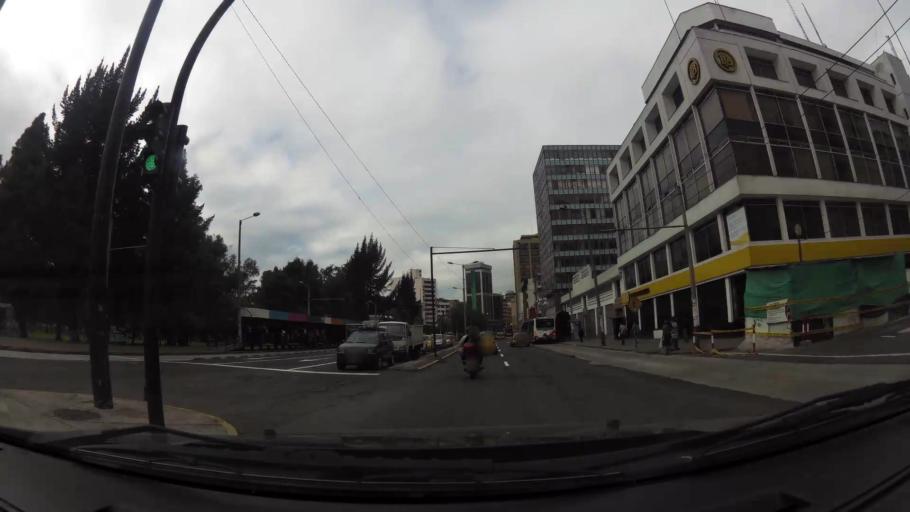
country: EC
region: Pichincha
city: Quito
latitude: -0.2090
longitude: -78.5004
